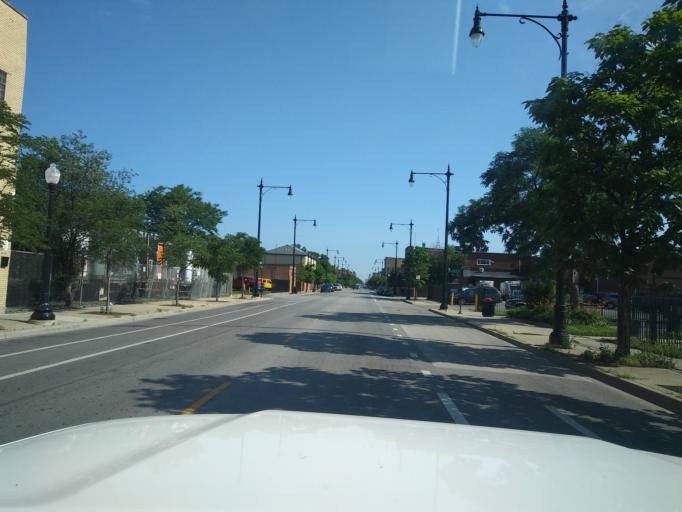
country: US
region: Illinois
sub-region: Cook County
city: Chicago
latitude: 41.8250
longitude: -87.6460
